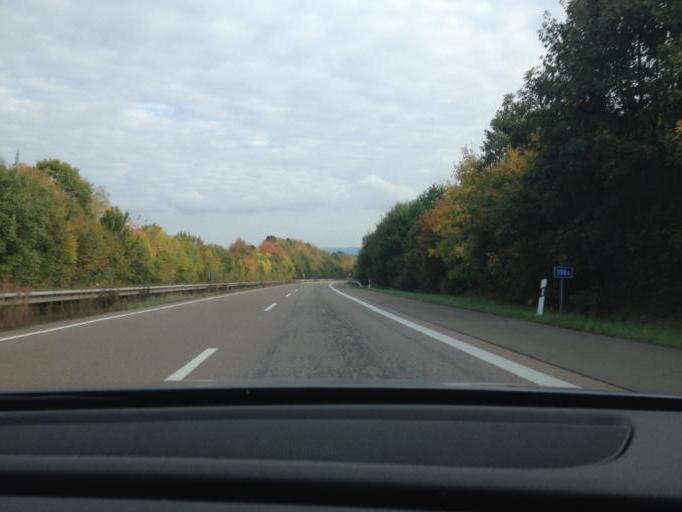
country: DE
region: Rheinland-Pfalz
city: Rehweiler
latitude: 49.4889
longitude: 7.4095
